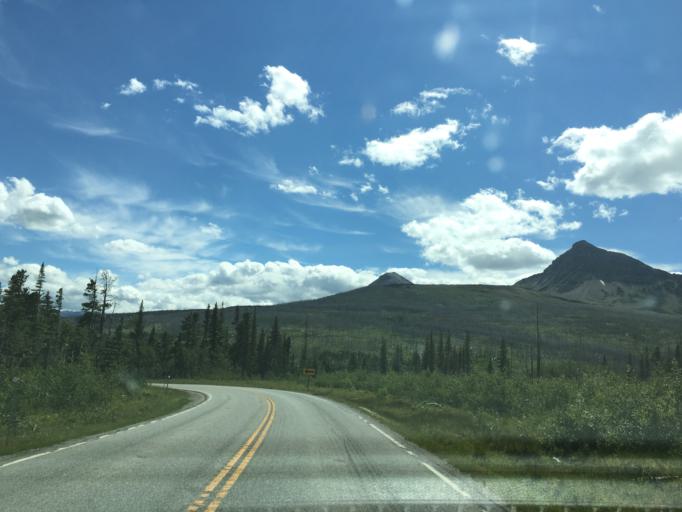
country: US
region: Montana
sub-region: Glacier County
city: North Browning
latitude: 48.6836
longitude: -113.3574
